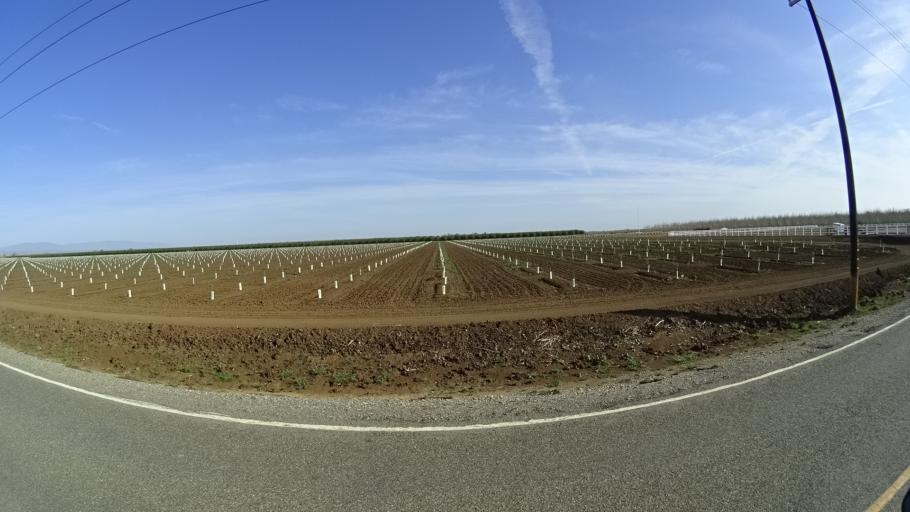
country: US
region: California
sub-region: Glenn County
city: Willows
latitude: 39.5388
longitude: -122.2331
